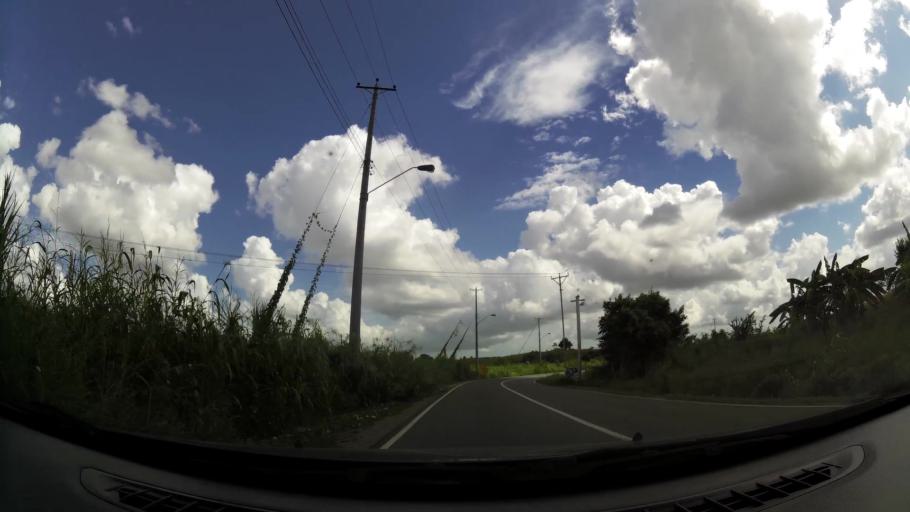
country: TT
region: Penal/Debe
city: Debe
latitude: 10.2306
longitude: -61.4810
